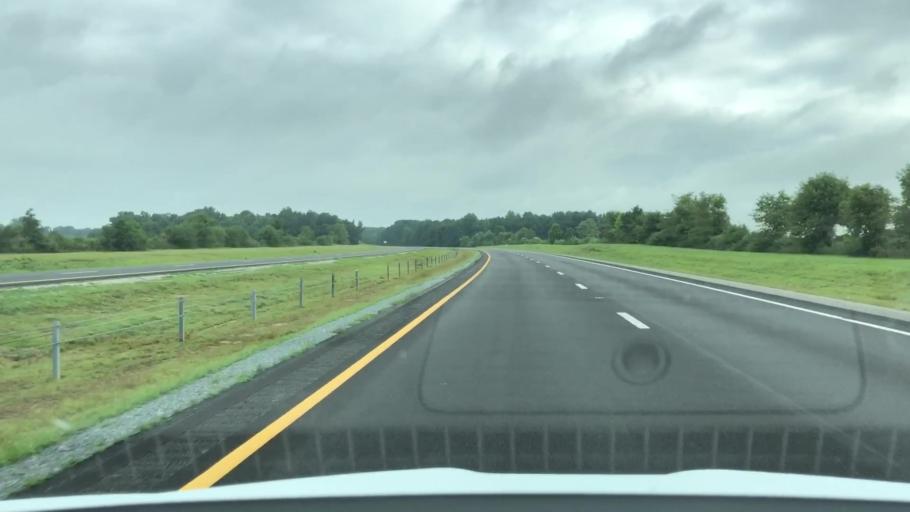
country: US
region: North Carolina
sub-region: Wayne County
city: Fremont
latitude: 35.5192
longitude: -77.9909
